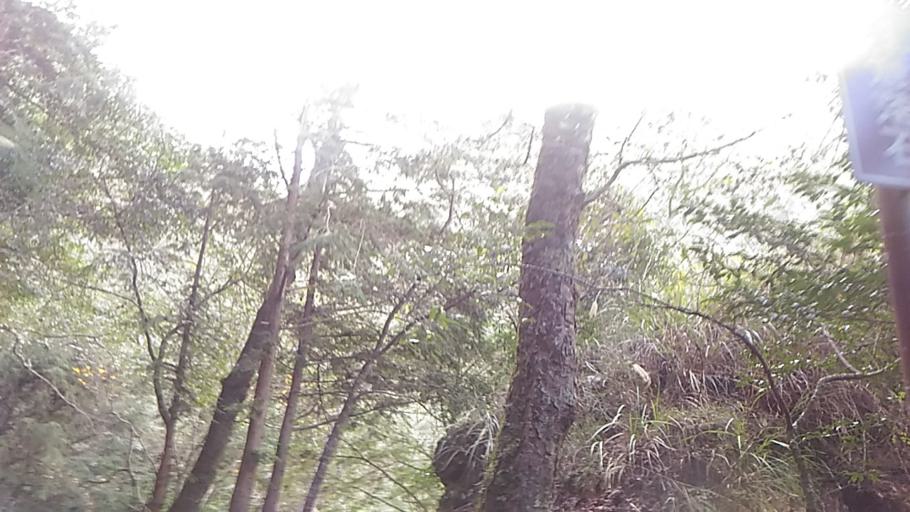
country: TW
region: Taiwan
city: Daxi
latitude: 24.4110
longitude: 121.3029
